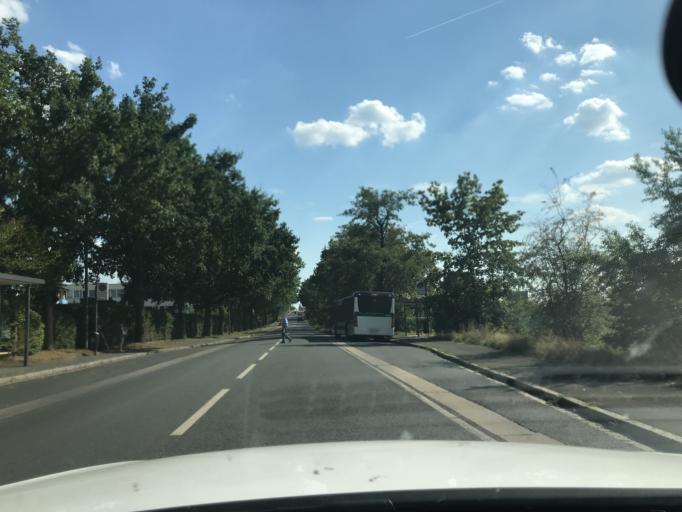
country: DE
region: Bavaria
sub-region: Regierungsbezirk Mittelfranken
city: Erlangen
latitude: 49.5653
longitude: 10.9857
